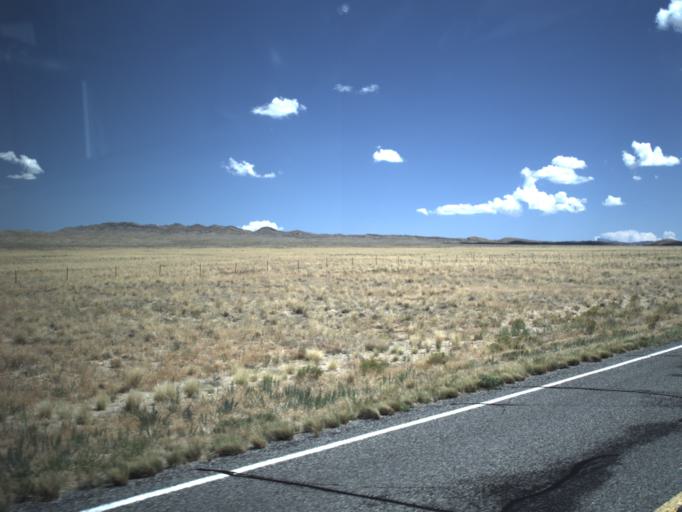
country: US
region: Nevada
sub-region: White Pine County
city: McGill
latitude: 39.0433
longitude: -113.8695
